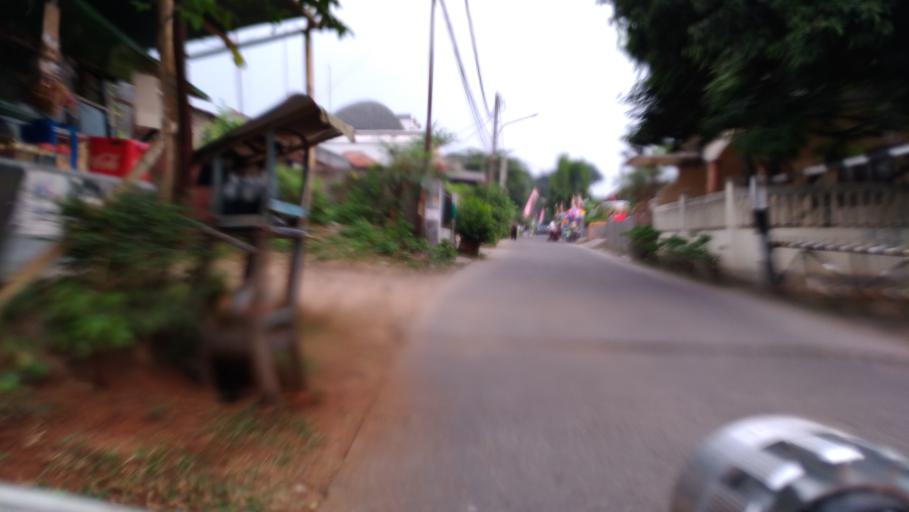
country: ID
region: West Java
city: Depok
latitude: -6.3639
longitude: 106.8659
